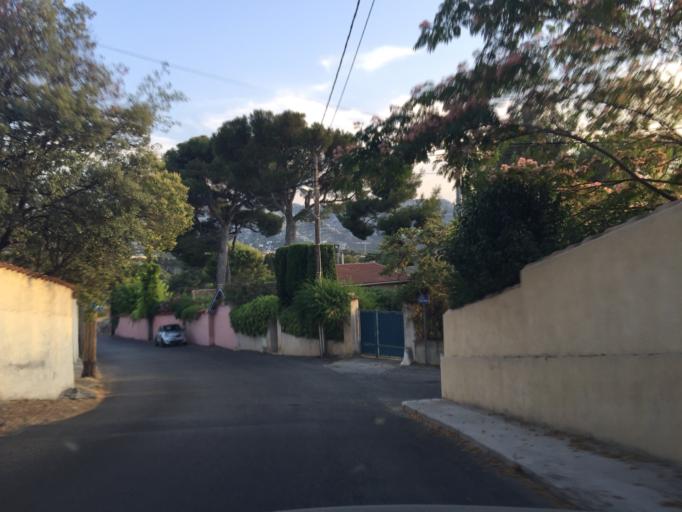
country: FR
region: Provence-Alpes-Cote d'Azur
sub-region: Departement des Bouches-du-Rhone
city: Marseille 09
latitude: 43.2408
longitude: 5.4135
